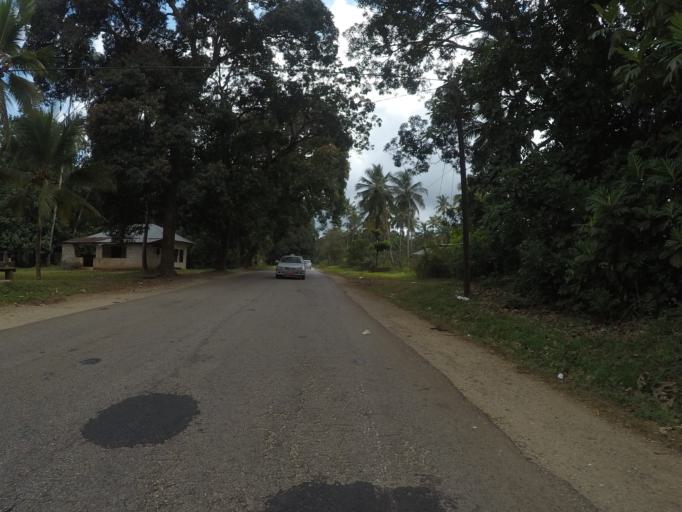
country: TZ
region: Zanzibar Central/South
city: Koani
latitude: -6.2127
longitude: 39.3238
